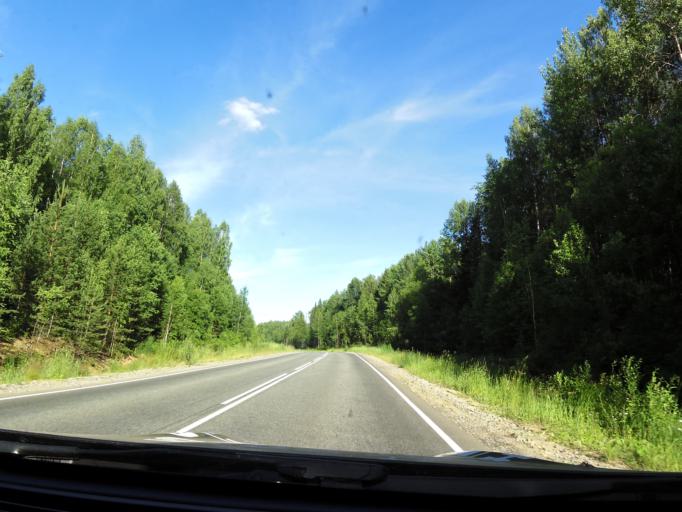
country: RU
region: Kirov
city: Chernaya Kholunitsa
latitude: 58.8588
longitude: 51.6275
